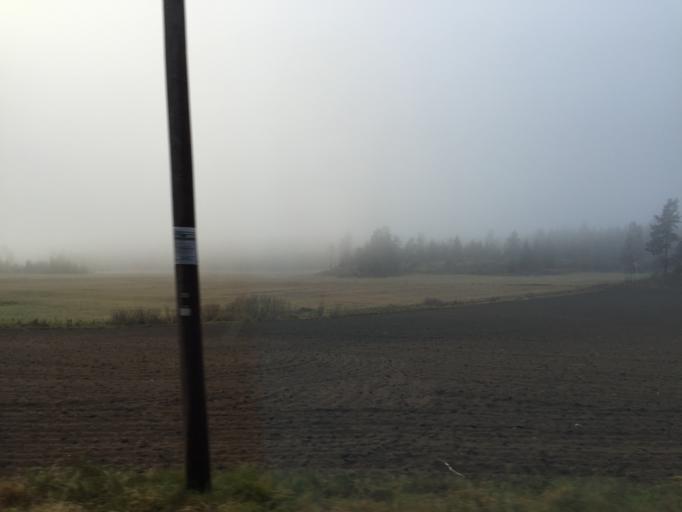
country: SE
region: Stockholm
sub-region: Nynashamns Kommun
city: Osmo
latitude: 59.0717
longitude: 17.8783
